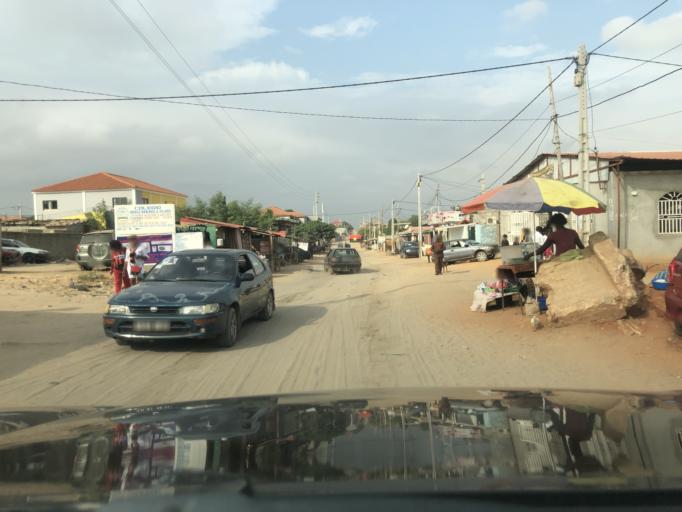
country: AO
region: Luanda
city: Luanda
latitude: -8.9332
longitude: 13.2320
